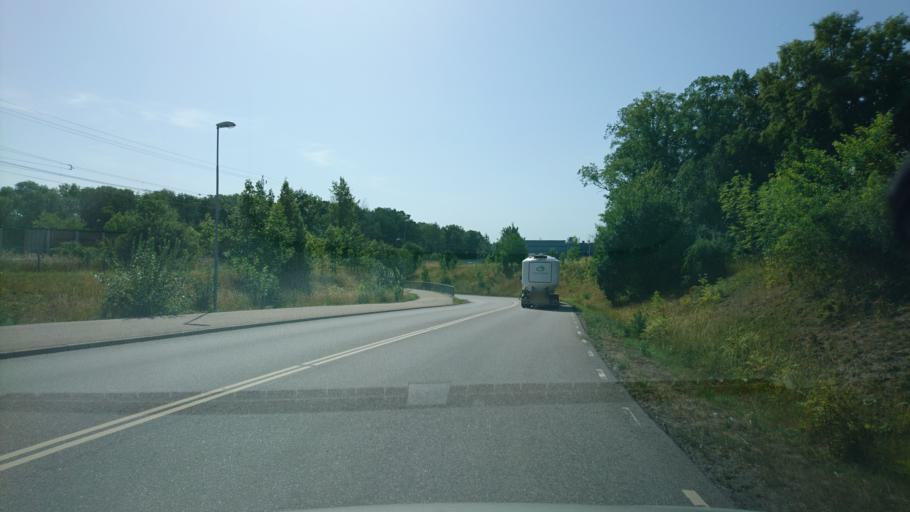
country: SE
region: Soedermanland
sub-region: Strangnas Kommun
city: Strangnas
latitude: 59.3623
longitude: 17.0383
